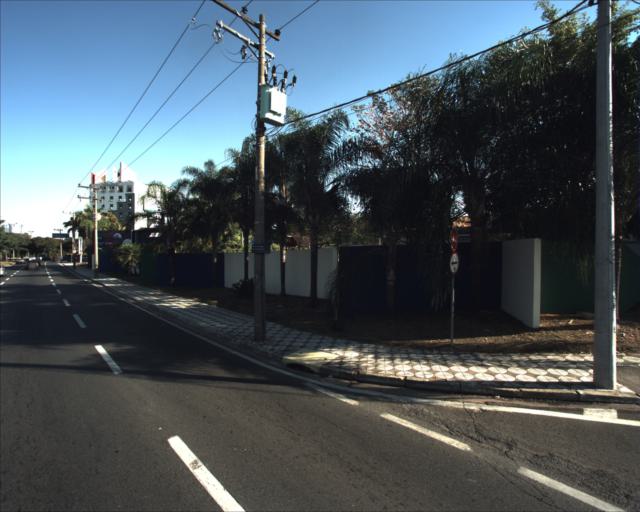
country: BR
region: Sao Paulo
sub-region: Sorocaba
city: Sorocaba
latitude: -23.4845
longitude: -47.4386
